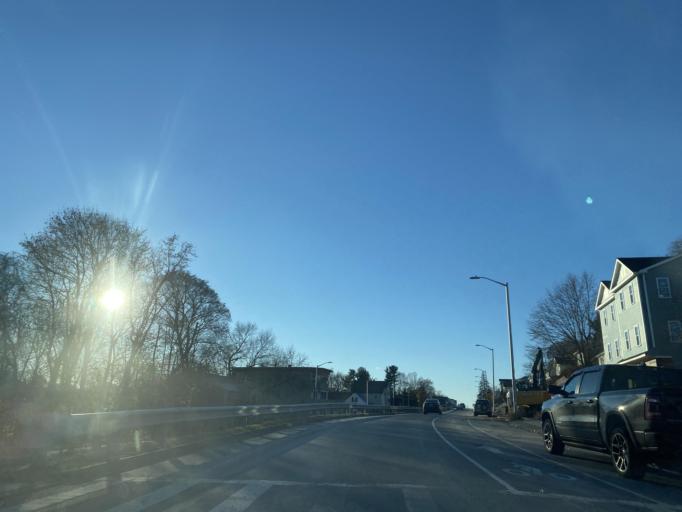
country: US
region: Massachusetts
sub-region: Worcester County
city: Hamilton
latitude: 42.2566
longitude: -71.7718
